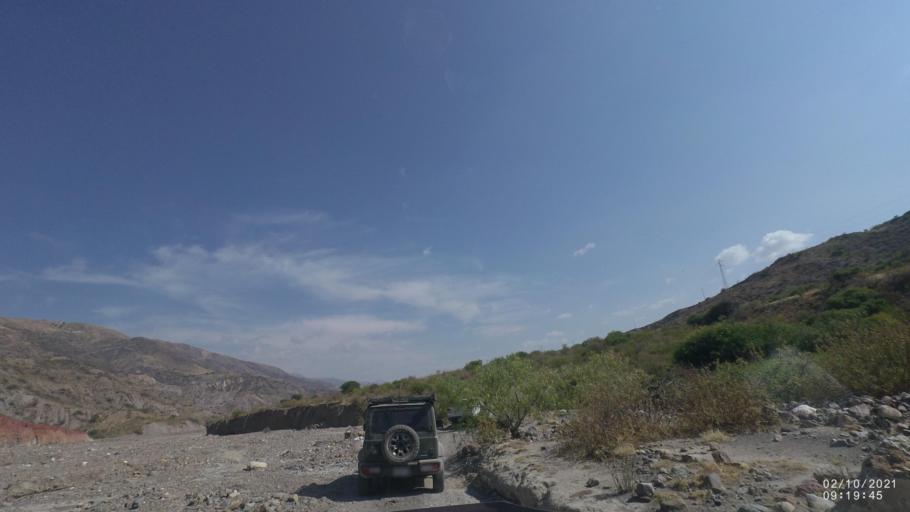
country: BO
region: Cochabamba
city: Irpa Irpa
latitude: -17.8755
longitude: -66.3067
